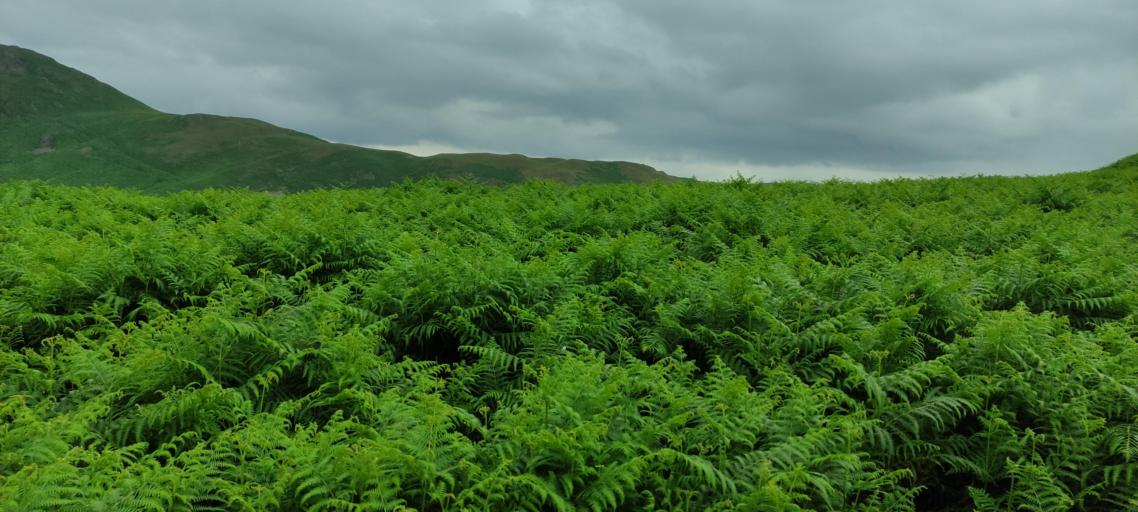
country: GB
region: England
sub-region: Cumbria
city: Ambleside
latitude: 54.5552
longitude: -2.8830
